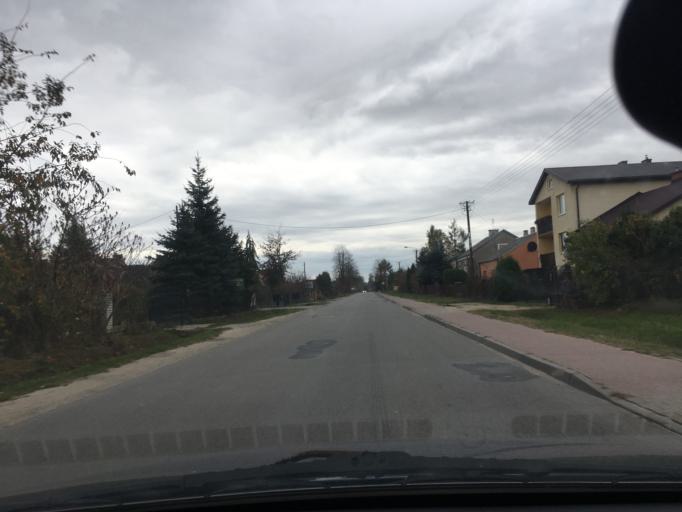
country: PL
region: Lodz Voivodeship
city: Zabia Wola
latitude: 52.0287
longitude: 20.6905
